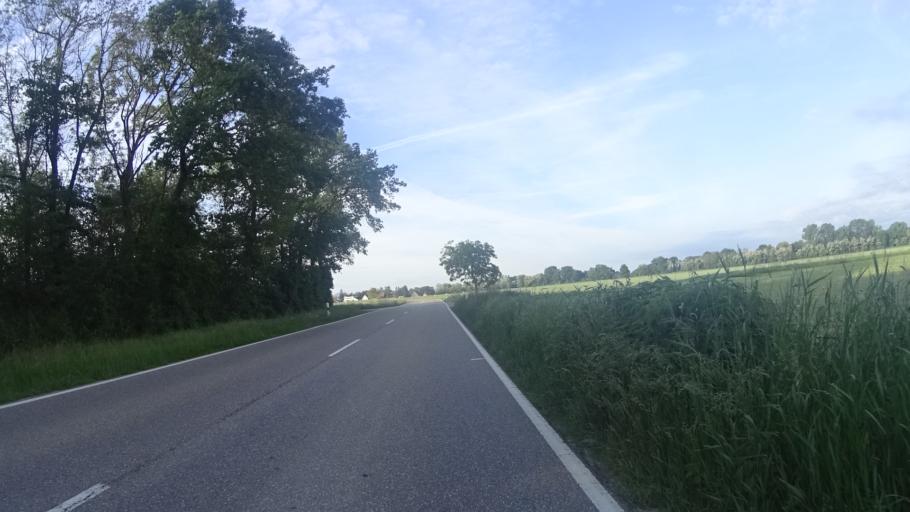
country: DE
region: Baden-Wuerttemberg
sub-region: Freiburg Region
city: Hartheim
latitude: 47.9742
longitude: 7.6441
